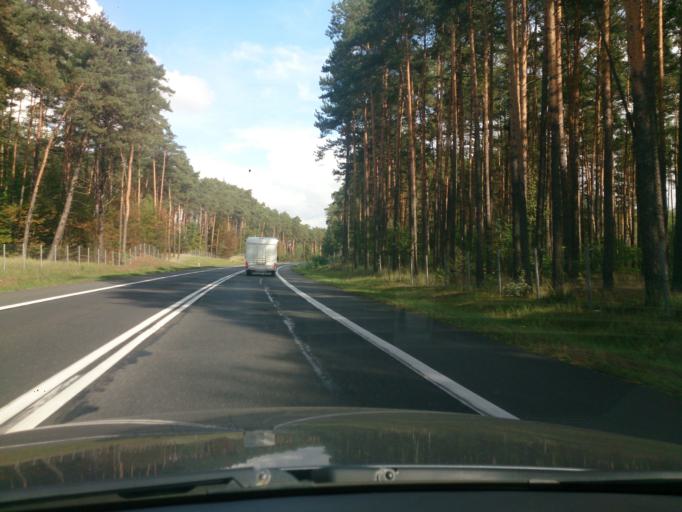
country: PL
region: Kujawsko-Pomorskie
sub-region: Powiat chelminski
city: Chelmno
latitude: 53.3978
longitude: 18.3507
